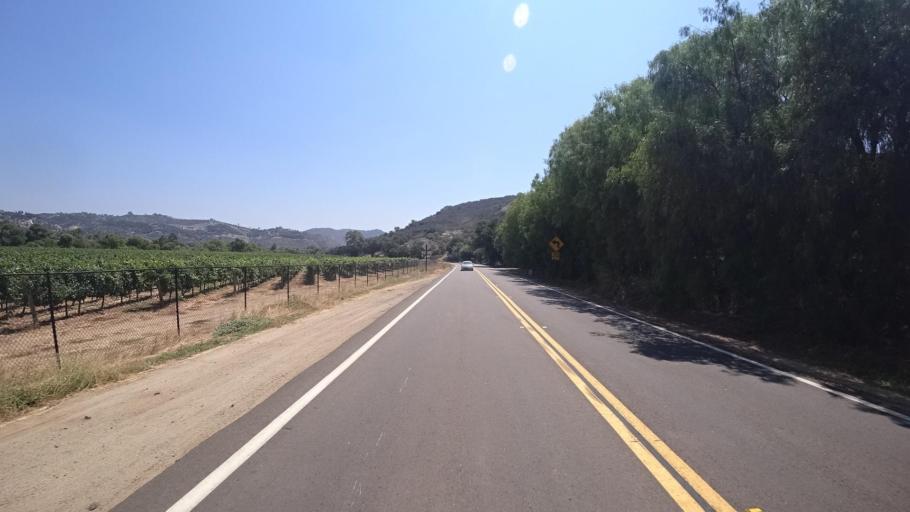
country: US
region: California
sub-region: San Diego County
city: Bonsall
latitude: 33.2735
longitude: -117.1828
